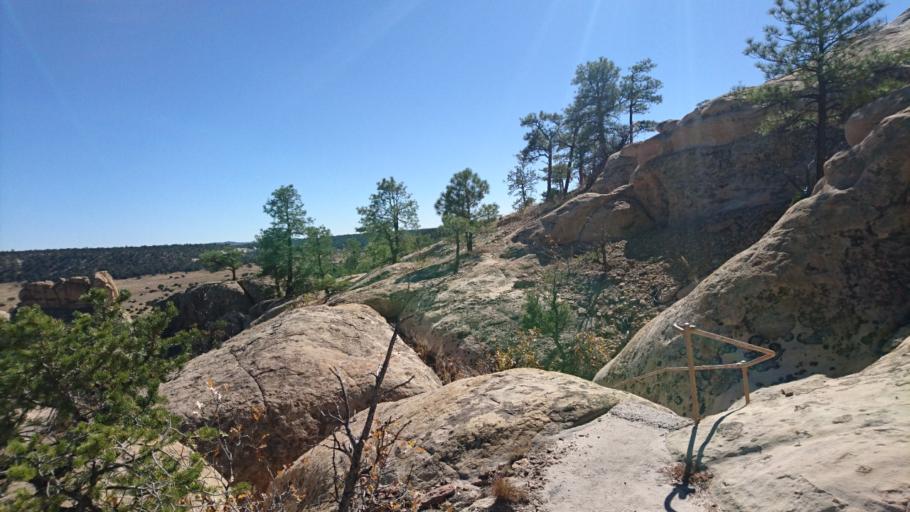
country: US
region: New Mexico
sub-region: McKinley County
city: Thoreau
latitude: 35.0370
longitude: -108.3526
